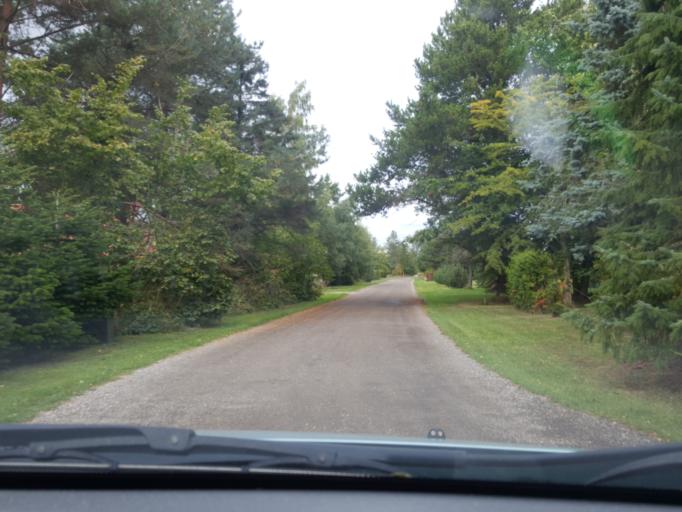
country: DK
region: Zealand
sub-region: Guldborgsund Kommune
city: Nykobing Falster
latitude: 54.6563
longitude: 11.9472
